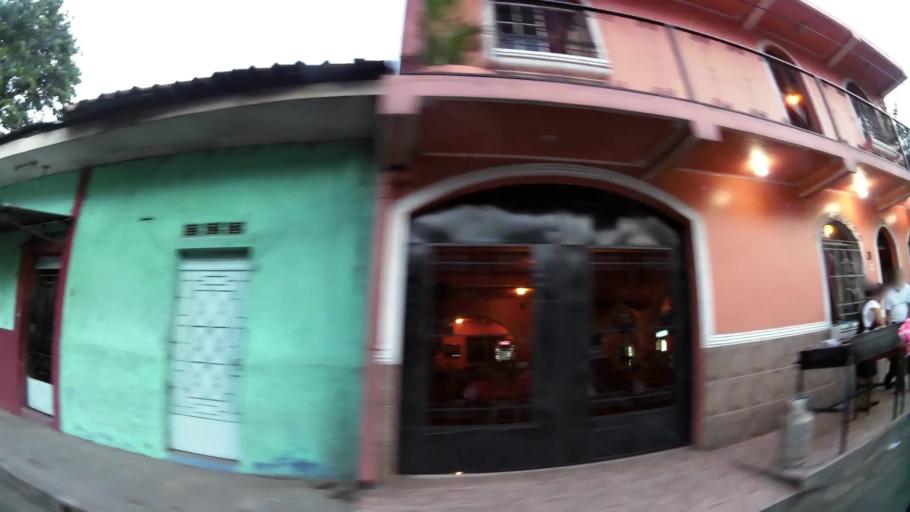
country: SV
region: San Vicente
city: San Vicente
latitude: 13.6411
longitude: -88.7856
